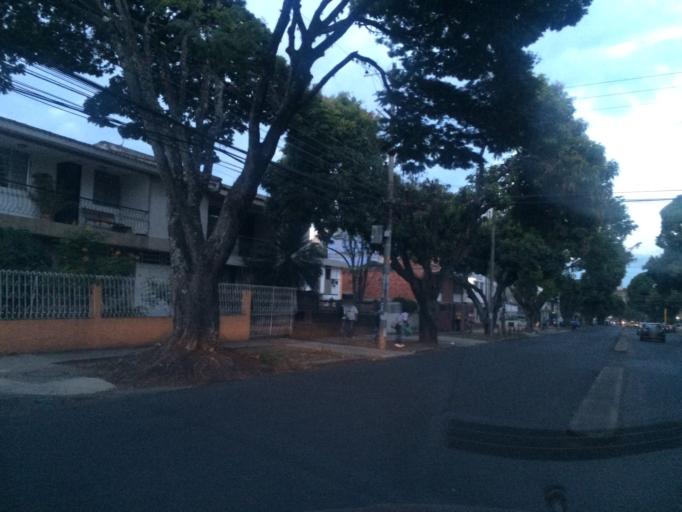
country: CO
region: Valle del Cauca
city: Cali
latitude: 3.4230
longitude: -76.5498
